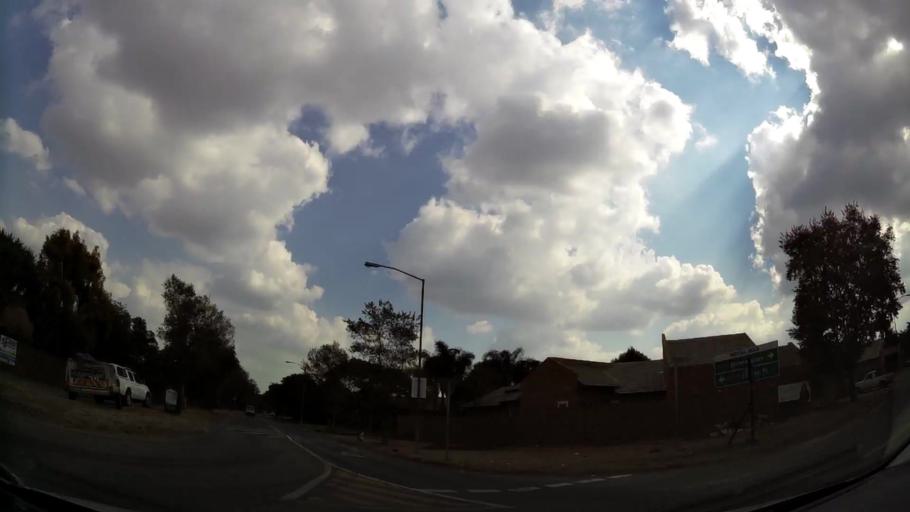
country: ZA
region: Gauteng
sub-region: City of Tshwane Metropolitan Municipality
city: Centurion
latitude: -25.8445
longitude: 28.2715
